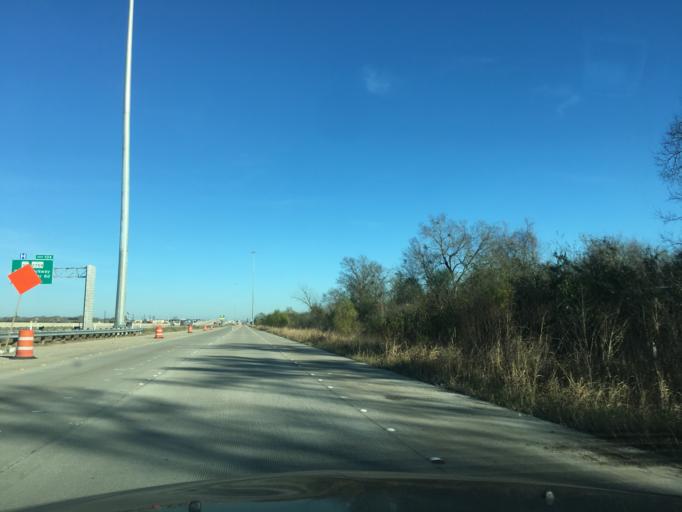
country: US
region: Texas
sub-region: Fort Bend County
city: Richmond
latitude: 29.5531
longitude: -95.7282
